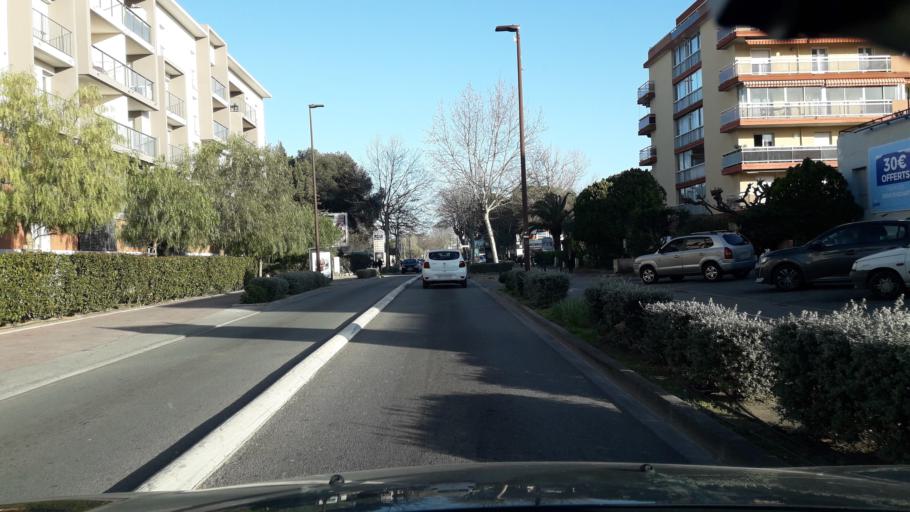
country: FR
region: Provence-Alpes-Cote d'Azur
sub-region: Departement du Var
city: Frejus
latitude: 43.4318
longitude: 6.7514
